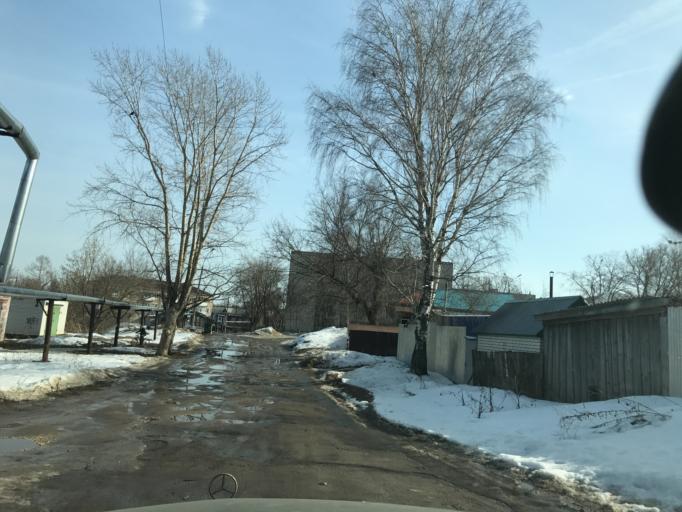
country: RU
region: Nizjnij Novgorod
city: Taremskoye
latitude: 55.9560
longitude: 43.0536
